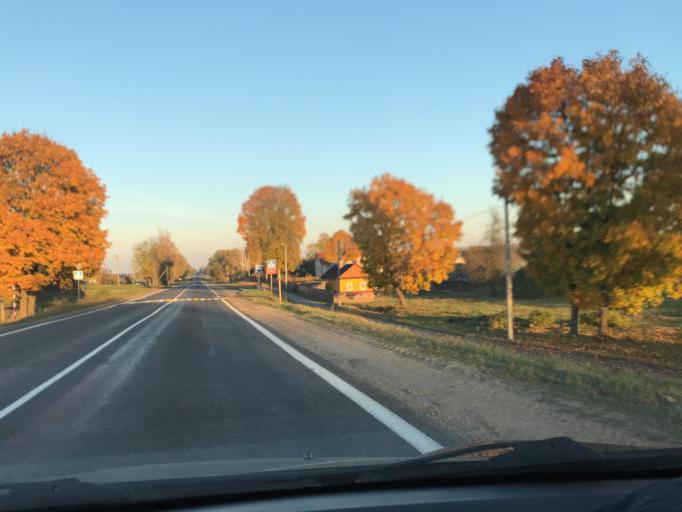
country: BY
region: Minsk
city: Staryya Darohi
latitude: 53.0546
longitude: 28.4191
